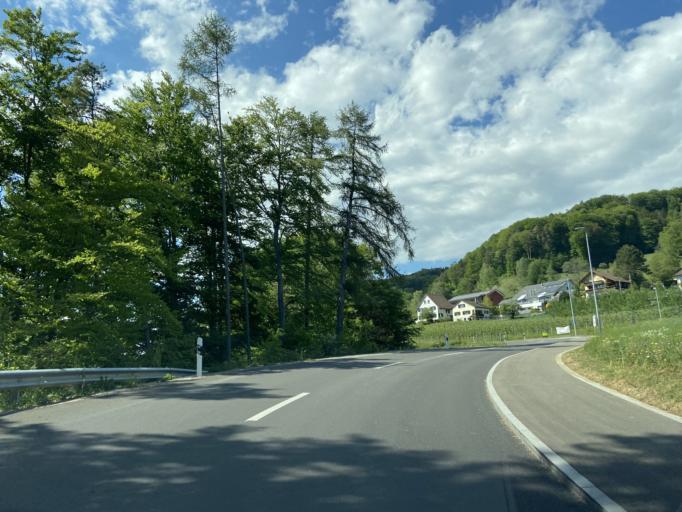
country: CH
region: Zurich
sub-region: Bezirk Winterthur
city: Pfungen
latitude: 47.5220
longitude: 8.6301
